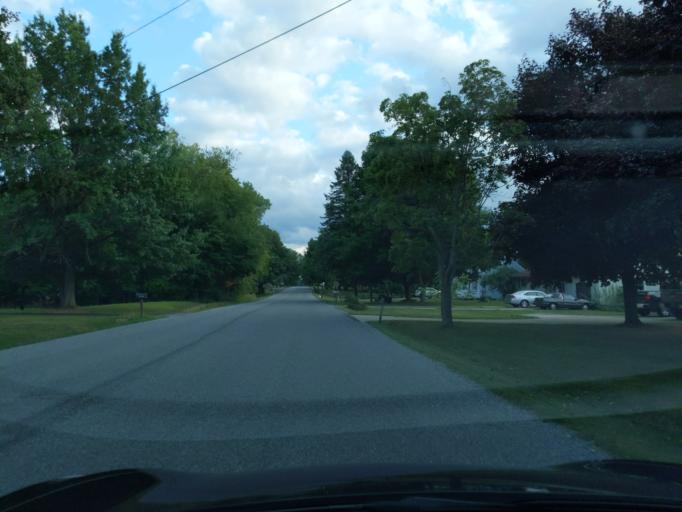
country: US
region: Michigan
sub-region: Ingham County
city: Holt
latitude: 42.6090
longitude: -84.5823
